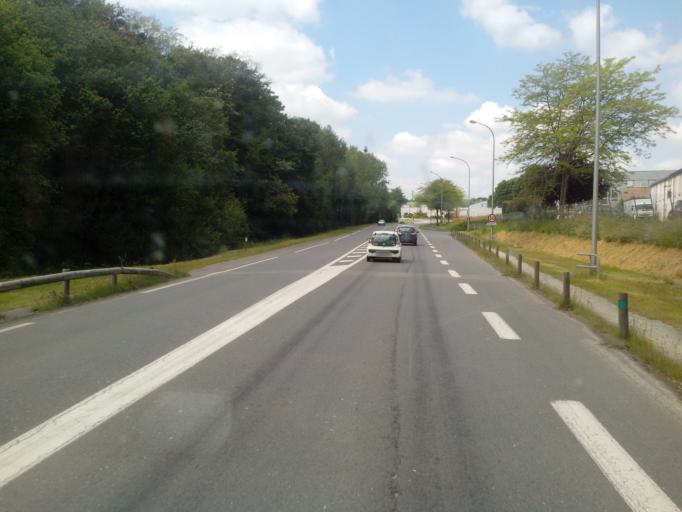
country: FR
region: Brittany
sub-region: Departement d'Ille-et-Vilaine
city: Lecousse
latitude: 48.3686
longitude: -1.2033
